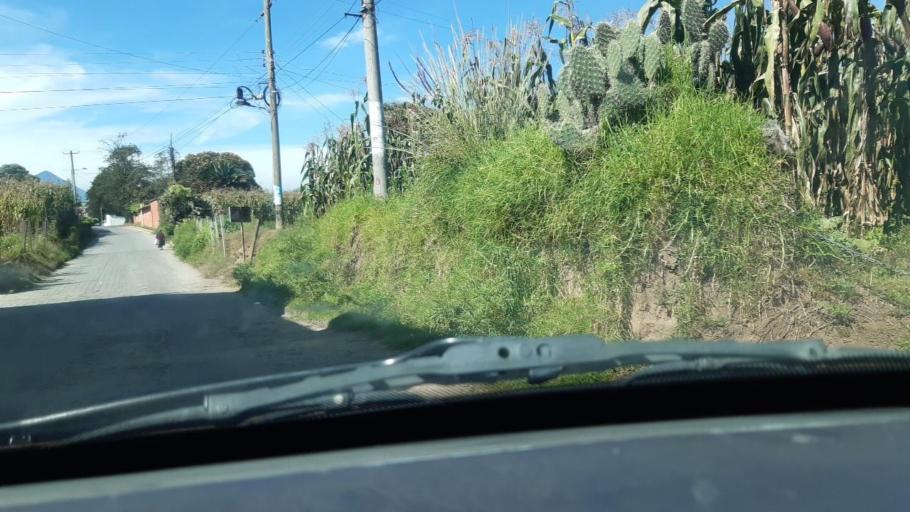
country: GT
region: Quetzaltenango
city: Salcaja
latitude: 14.8891
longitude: -91.4511
